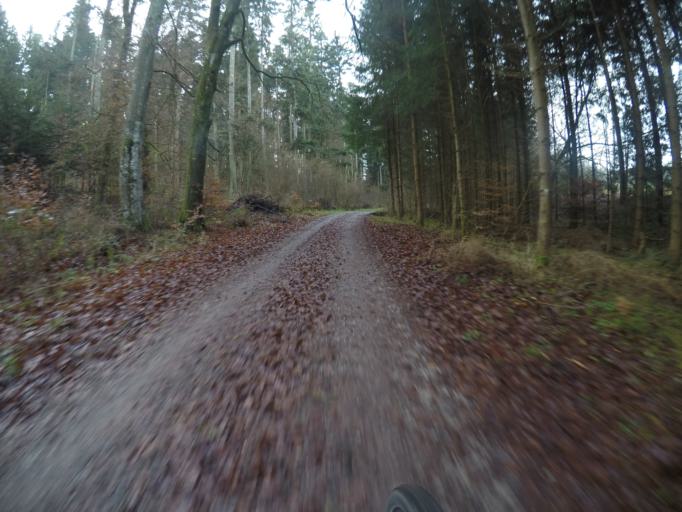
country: DE
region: Baden-Wuerttemberg
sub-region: Regierungsbezirk Stuttgart
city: Deckenpfronn
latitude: 48.6682
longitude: 8.8296
